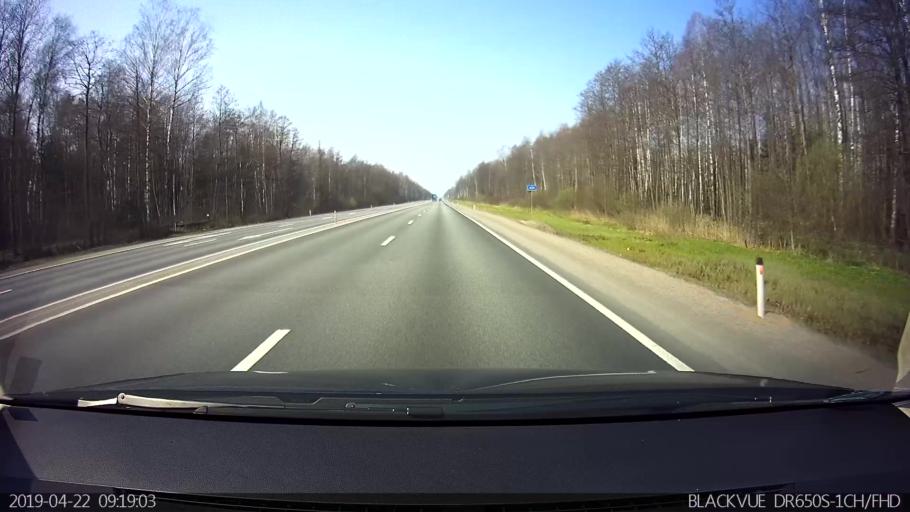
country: RU
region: Smolensk
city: Golynki
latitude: 54.7490
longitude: 31.4753
